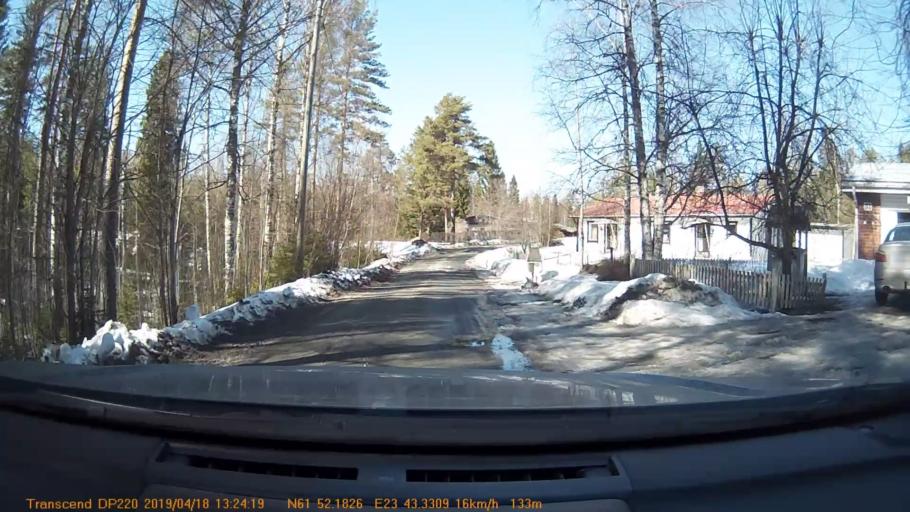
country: FI
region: Pirkanmaa
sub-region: Tampere
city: Kuru
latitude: 61.8697
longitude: 23.7223
